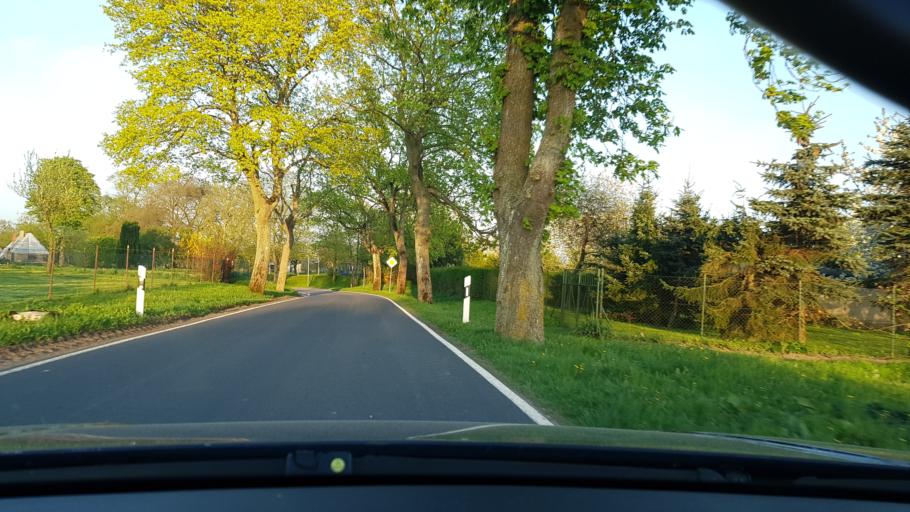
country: DE
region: Mecklenburg-Vorpommern
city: Alt-Sanitz
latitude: 53.8942
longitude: 13.5672
